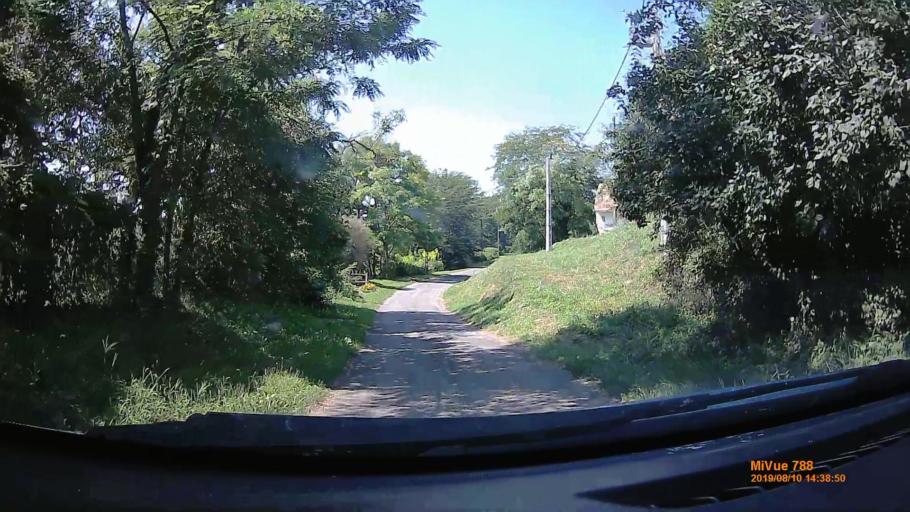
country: HU
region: Somogy
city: Somogyvar
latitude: 46.5679
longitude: 17.6808
